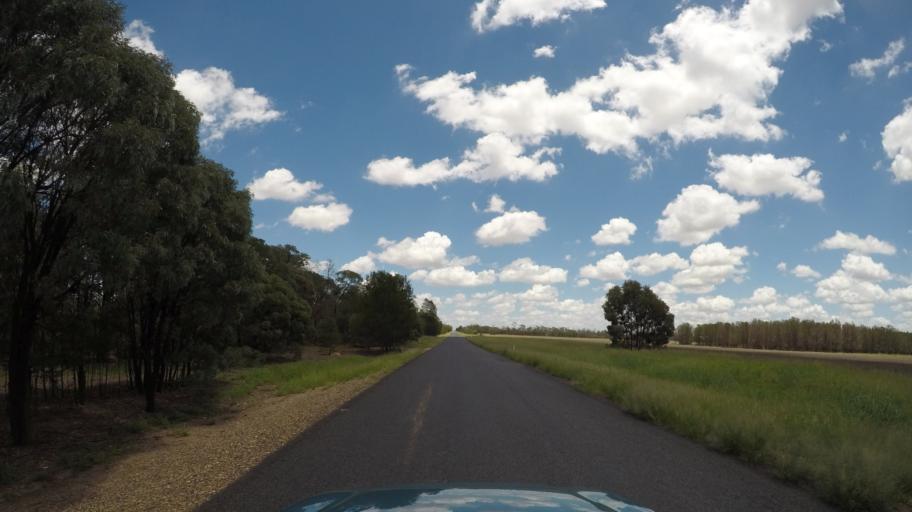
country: AU
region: Queensland
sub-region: Goondiwindi
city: Goondiwindi
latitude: -28.1701
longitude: 150.2115
